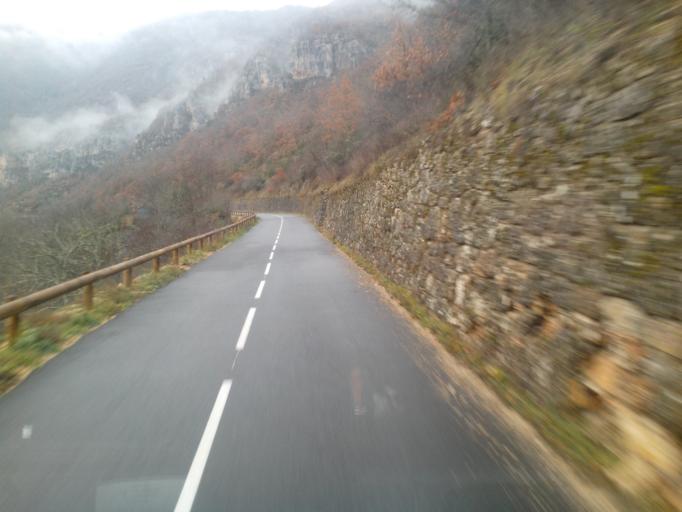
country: FR
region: Languedoc-Roussillon
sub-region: Departement de la Lozere
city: La Canourgue
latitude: 44.3026
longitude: 3.3109
